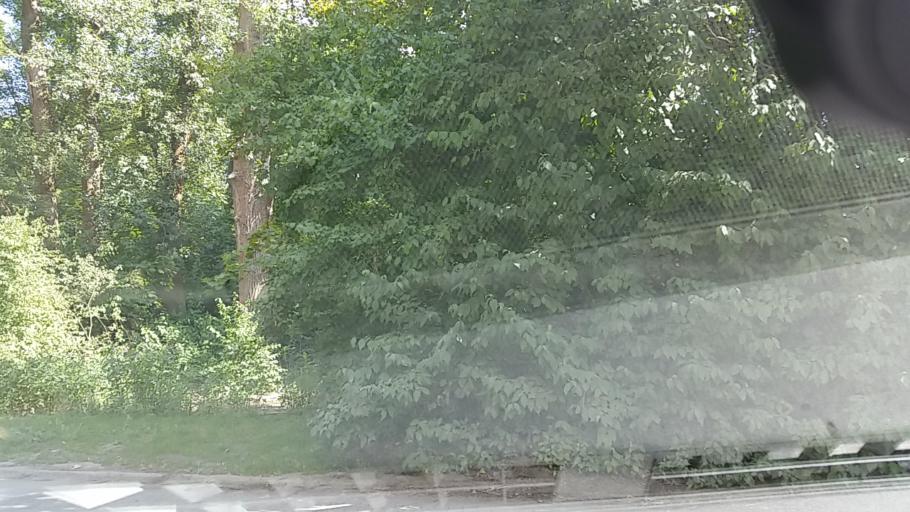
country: DE
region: Lower Saxony
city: Hannover
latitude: 52.3397
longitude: 9.7483
